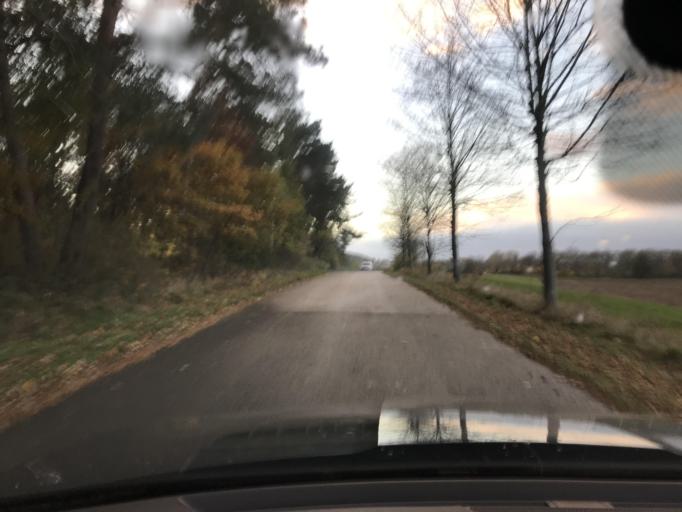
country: DE
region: Saxony-Anhalt
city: Langenstein
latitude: 51.8450
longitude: 11.0196
